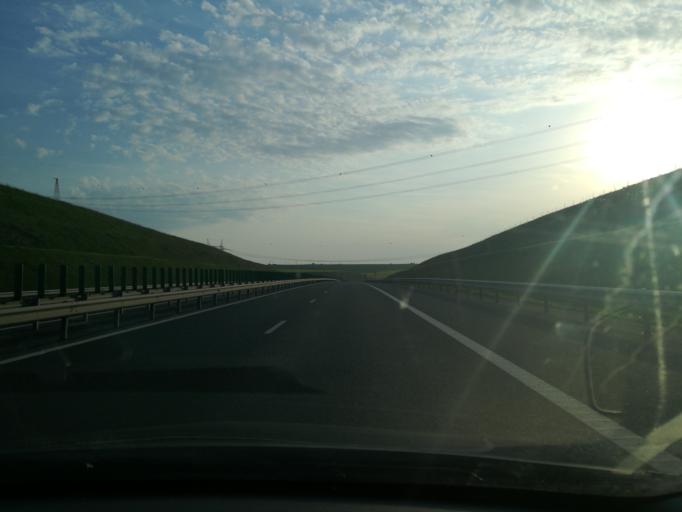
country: RO
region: Constanta
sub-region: Comuna Saligny
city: Faclia
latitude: 44.2442
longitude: 28.1171
